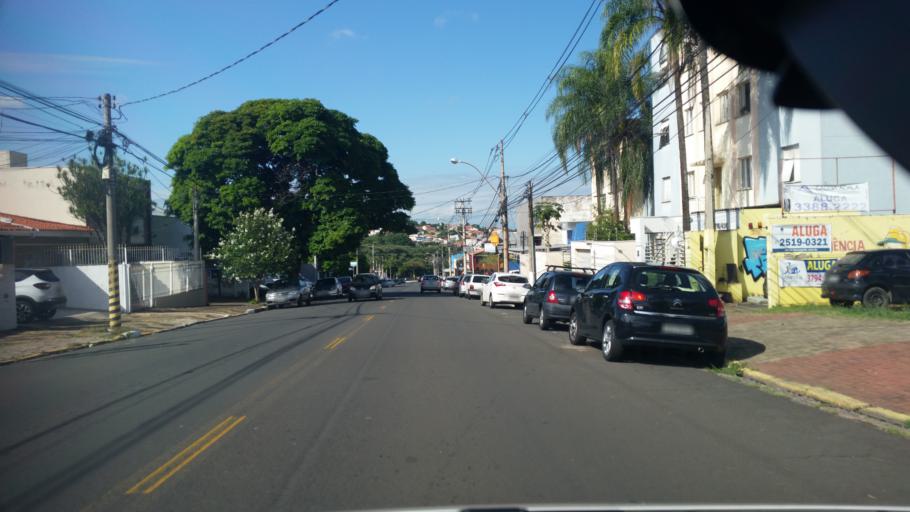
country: BR
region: Sao Paulo
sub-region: Campinas
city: Campinas
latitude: -22.8779
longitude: -47.0490
